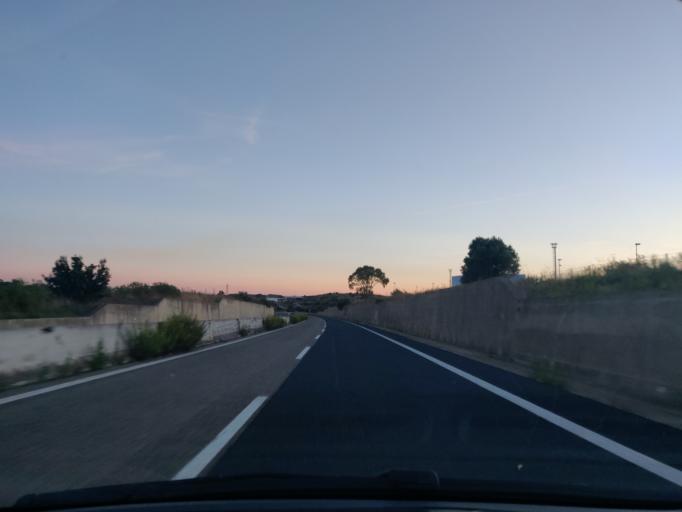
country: IT
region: Latium
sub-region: Citta metropolitana di Roma Capitale
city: Aurelia
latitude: 42.1260
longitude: 11.7914
